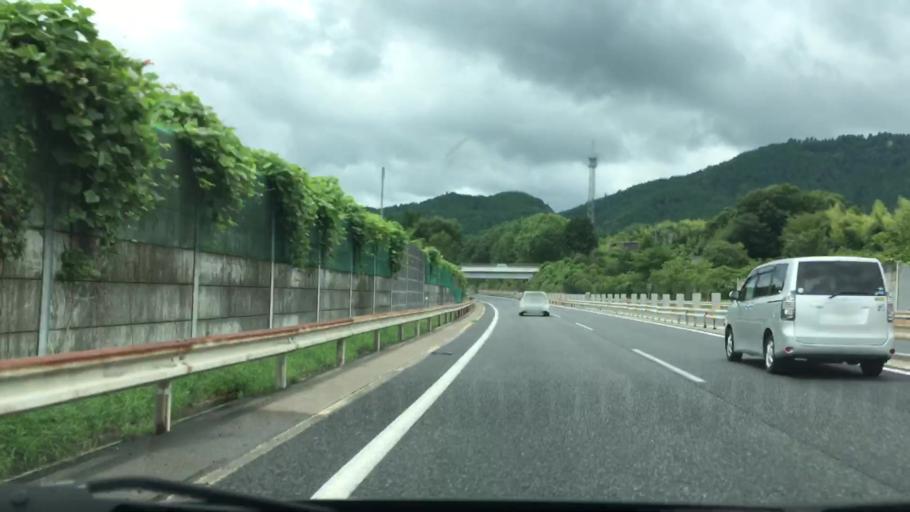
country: JP
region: Okayama
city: Takahashi
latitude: 35.0207
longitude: 133.7335
